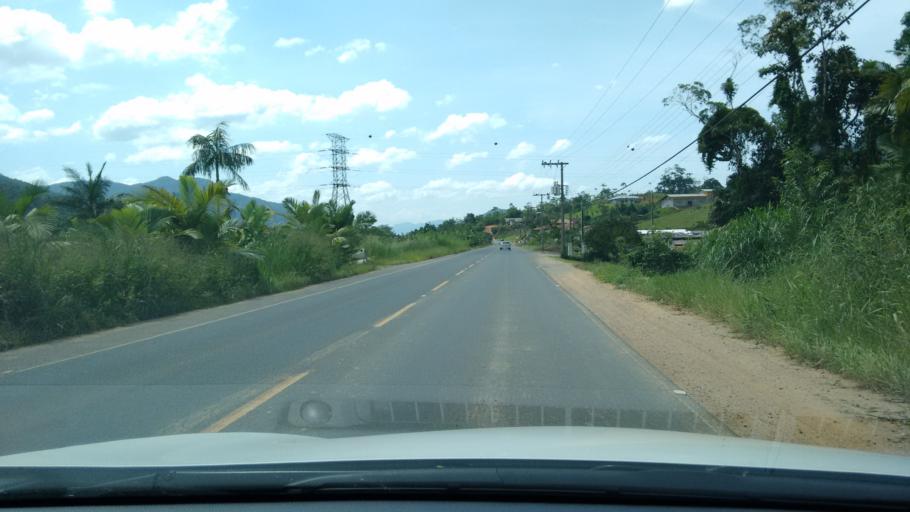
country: BR
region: Santa Catarina
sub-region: Rodeio
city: Gavea
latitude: -26.8627
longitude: -49.3351
